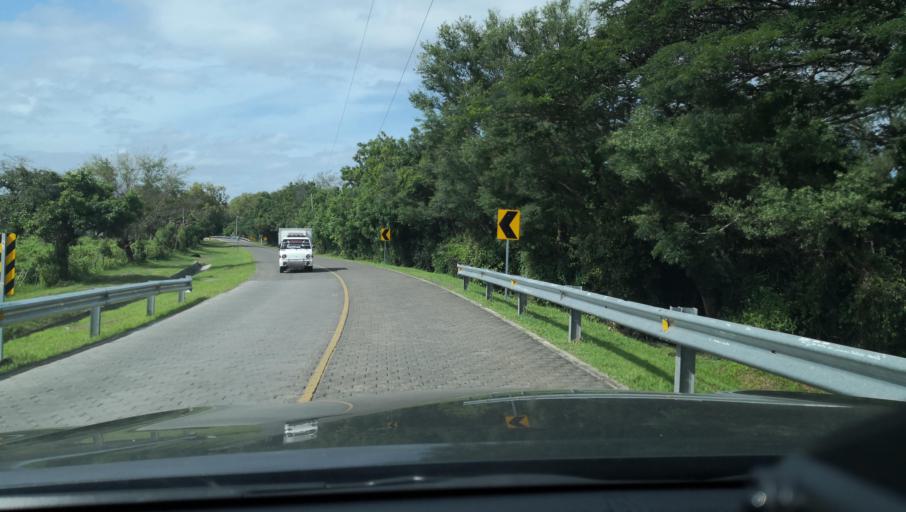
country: NI
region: Masaya
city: Tisma
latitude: 12.0932
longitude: -85.8966
